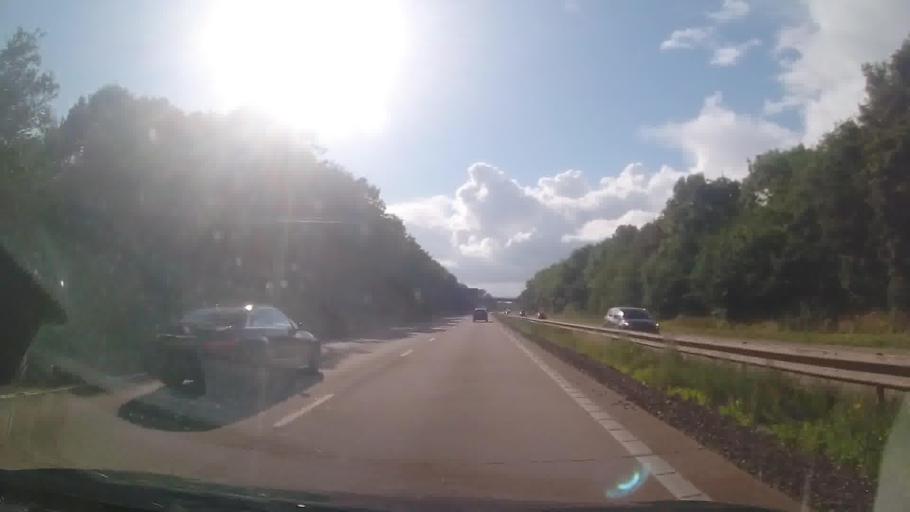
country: GB
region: England
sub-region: Shropshire
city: Albrighton
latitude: 52.6507
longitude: -2.2588
